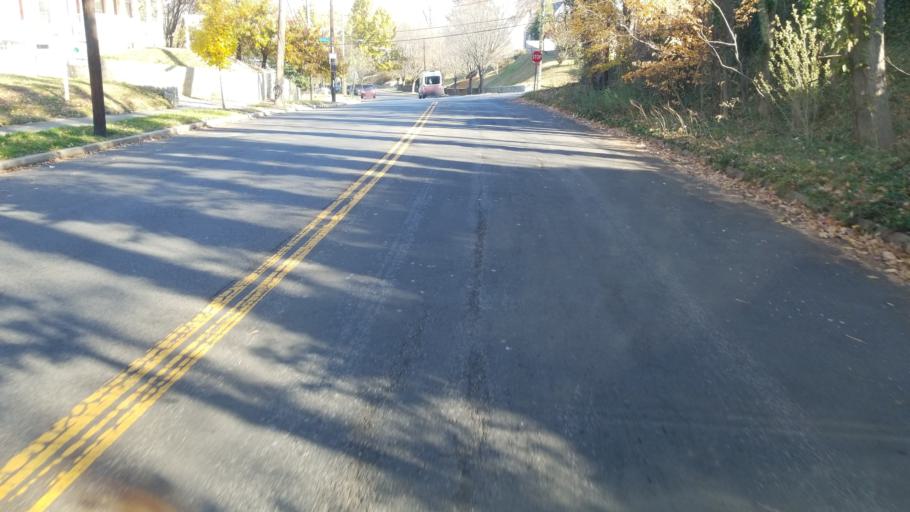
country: US
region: Maryland
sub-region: Prince George's County
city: Coral Hills
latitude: 38.8734
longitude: -76.9372
